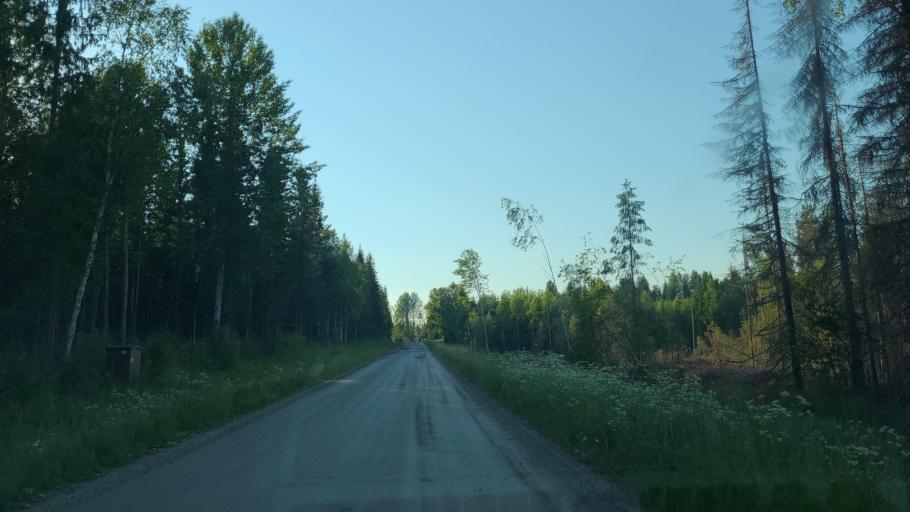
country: SE
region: Vaesterbotten
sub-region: Skelleftea Kommun
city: Burea
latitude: 64.4079
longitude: 21.3592
